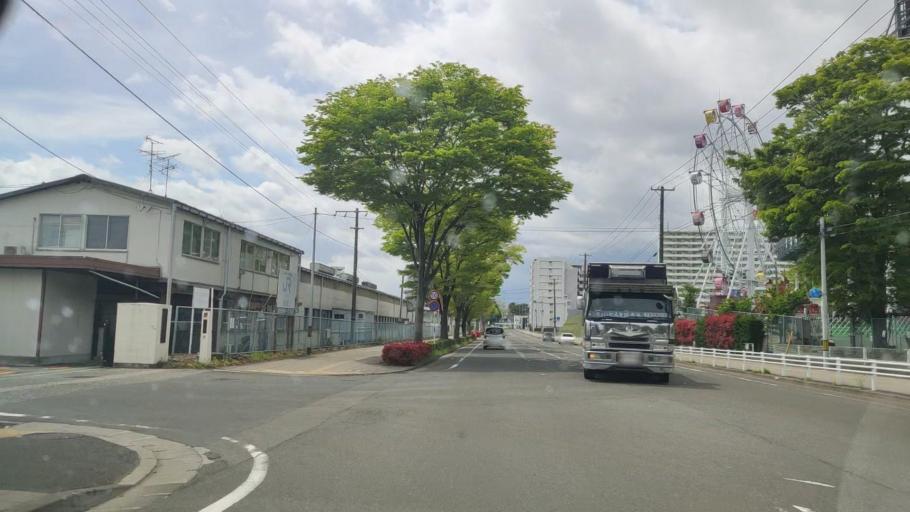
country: JP
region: Miyagi
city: Sendai-shi
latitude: 38.2563
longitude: 140.9045
